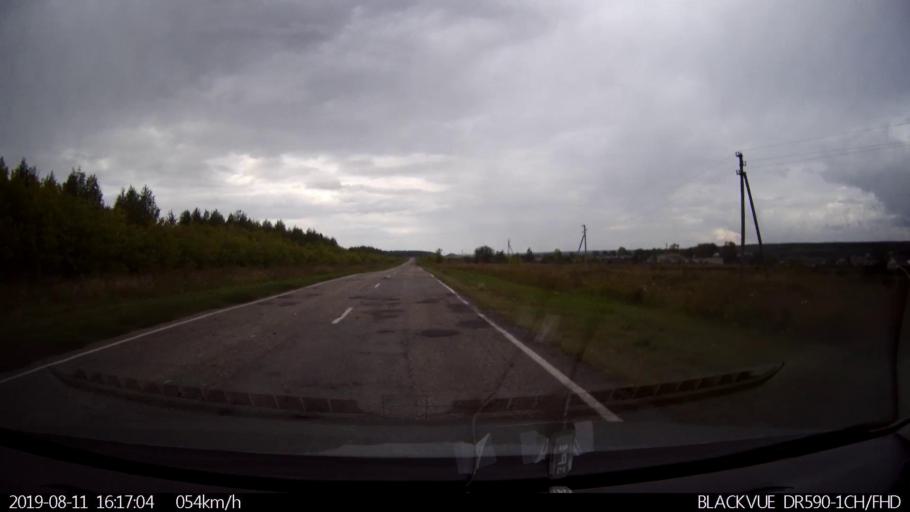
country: RU
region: Ulyanovsk
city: Mayna
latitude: 54.0455
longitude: 47.6179
